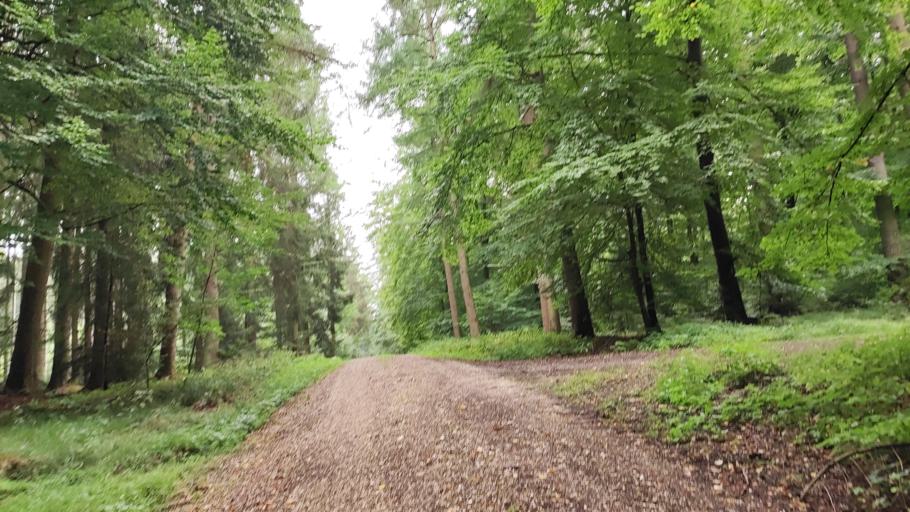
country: DE
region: Bavaria
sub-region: Swabia
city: Landensberg
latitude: 48.4298
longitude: 10.5138
